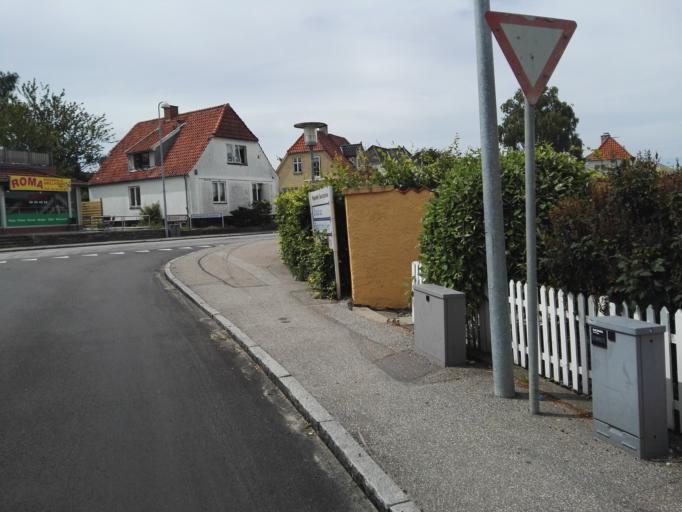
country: DK
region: Capital Region
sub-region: Hillerod Kommune
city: Skaevinge
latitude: 55.9086
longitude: 12.1498
